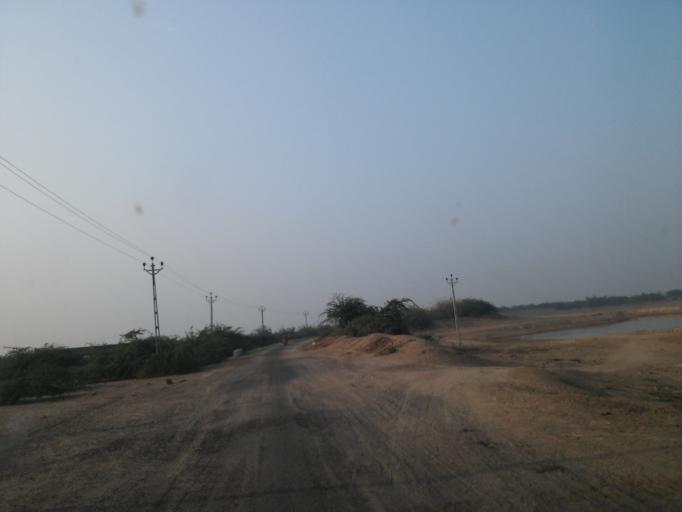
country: IN
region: Gujarat
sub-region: Kachchh
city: Mandvi
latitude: 22.8317
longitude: 69.3880
